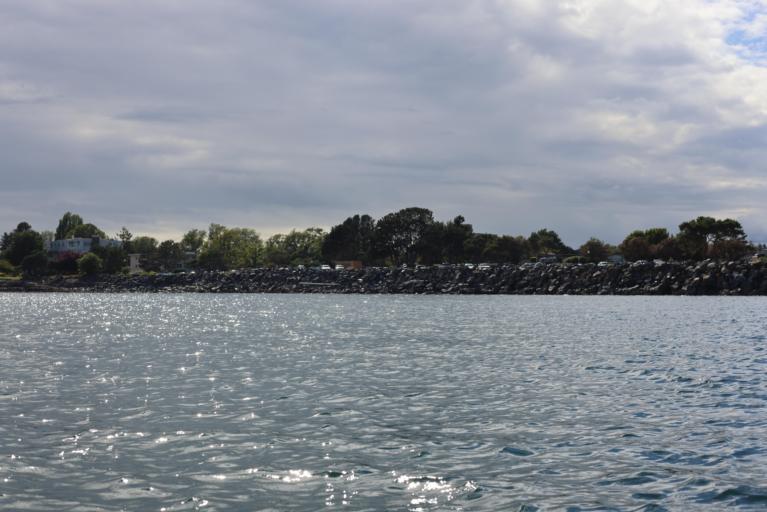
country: CA
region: British Columbia
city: Oak Bay
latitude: 48.4243
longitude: -123.2978
